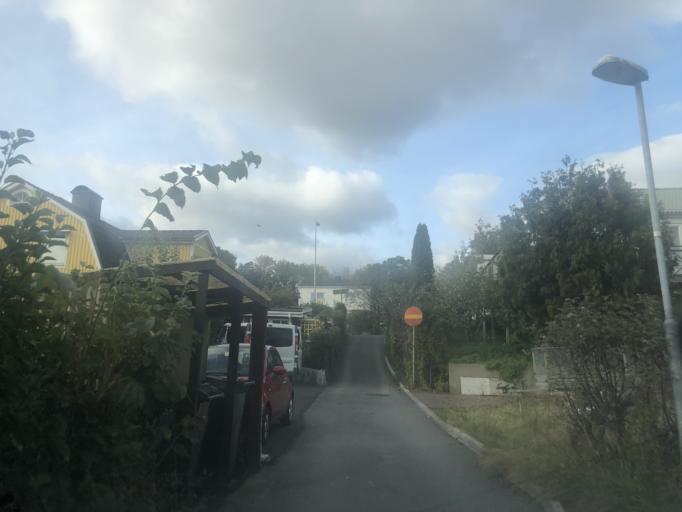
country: SE
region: Vaestra Goetaland
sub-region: Goteborg
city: Majorna
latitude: 57.6344
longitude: 11.9407
